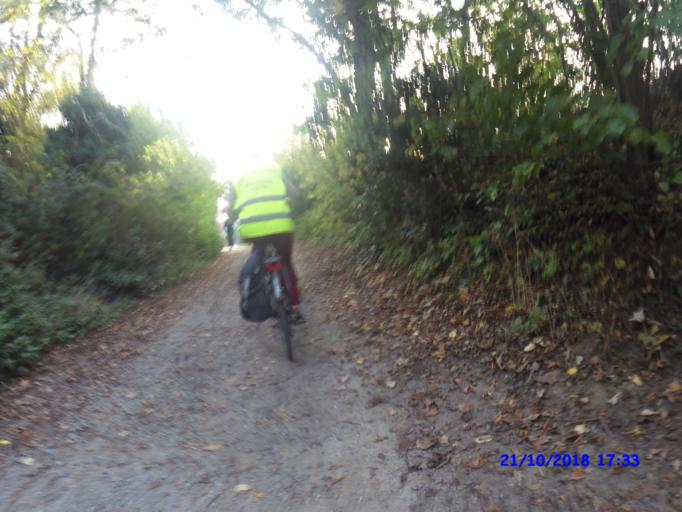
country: BE
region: Flanders
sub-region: Provincie Vlaams-Brabant
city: Kraainem
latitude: 50.8500
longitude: 4.4464
